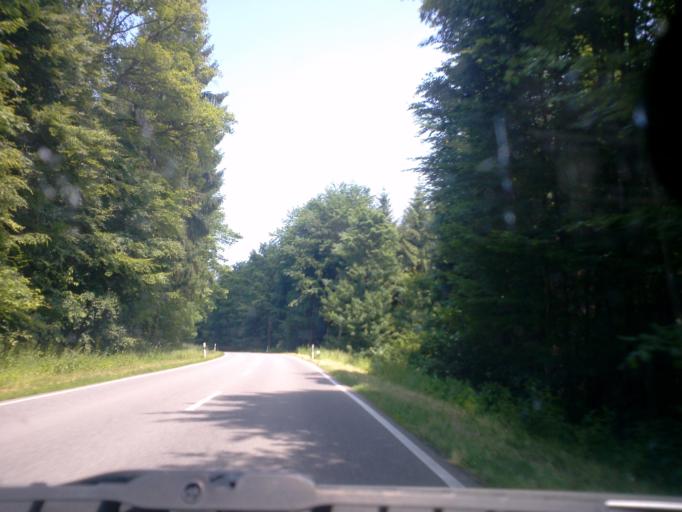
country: DE
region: Baden-Wuerttemberg
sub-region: Karlsruhe Region
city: Eisingen
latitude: 48.9942
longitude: 8.6556
